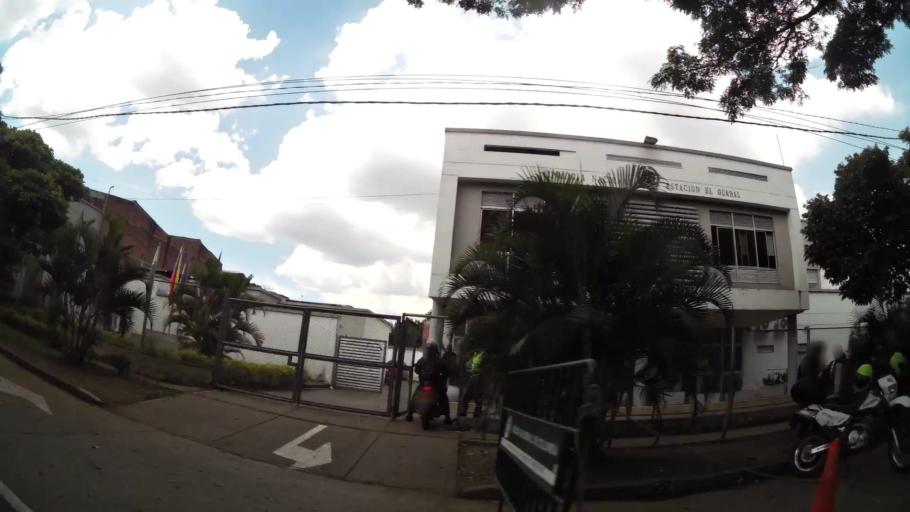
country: CO
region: Valle del Cauca
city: Cali
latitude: 3.4129
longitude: -76.5274
